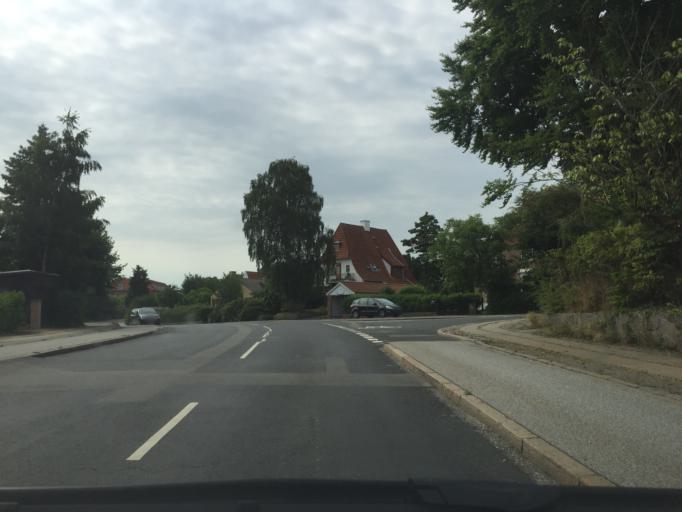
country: DK
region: Capital Region
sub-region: Gentofte Kommune
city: Charlottenlund
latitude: 55.7480
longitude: 12.5464
